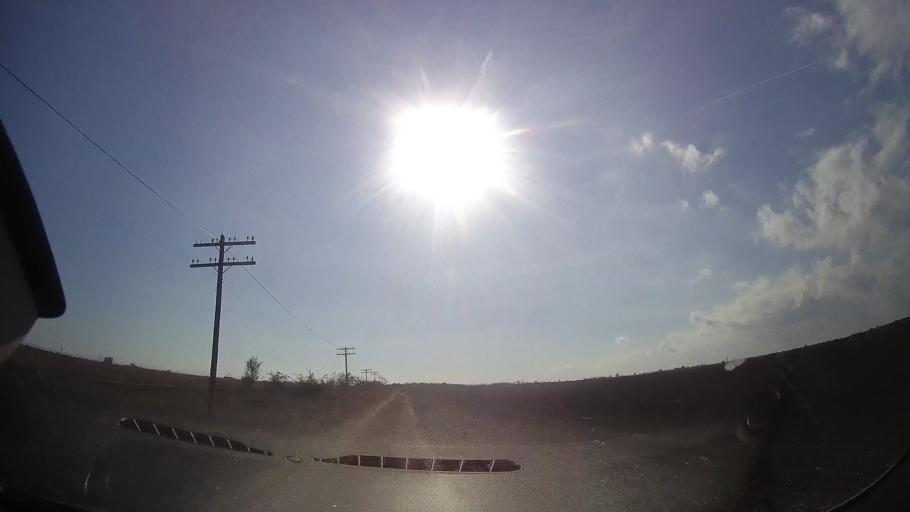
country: RO
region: Constanta
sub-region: Comuna Tuzla
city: Tuzla
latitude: 43.9794
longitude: 28.6443
